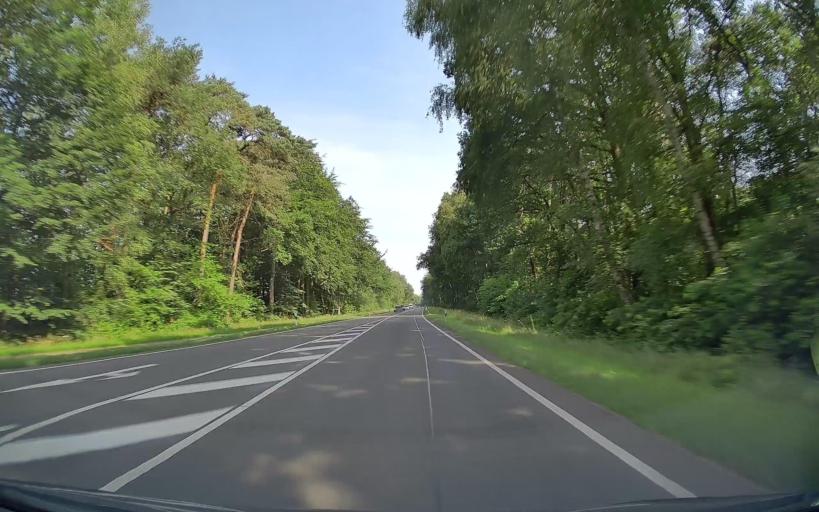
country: DE
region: Lower Saxony
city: Molbergen
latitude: 52.9272
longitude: 7.9503
